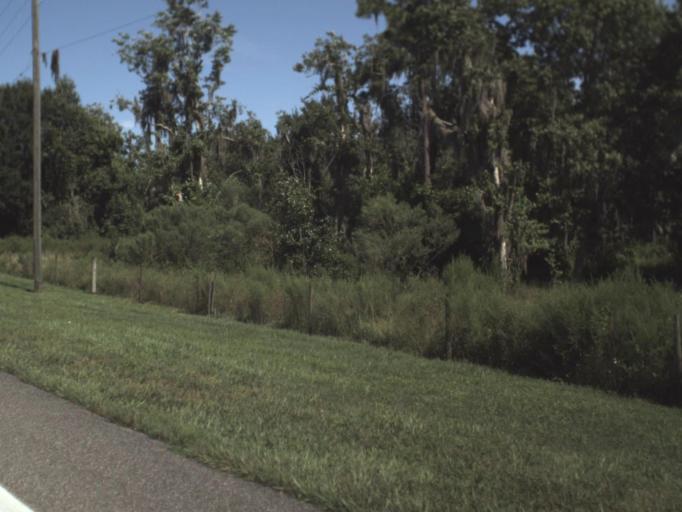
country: US
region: Florida
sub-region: Polk County
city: Polk City
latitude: 28.1675
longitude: -81.8055
